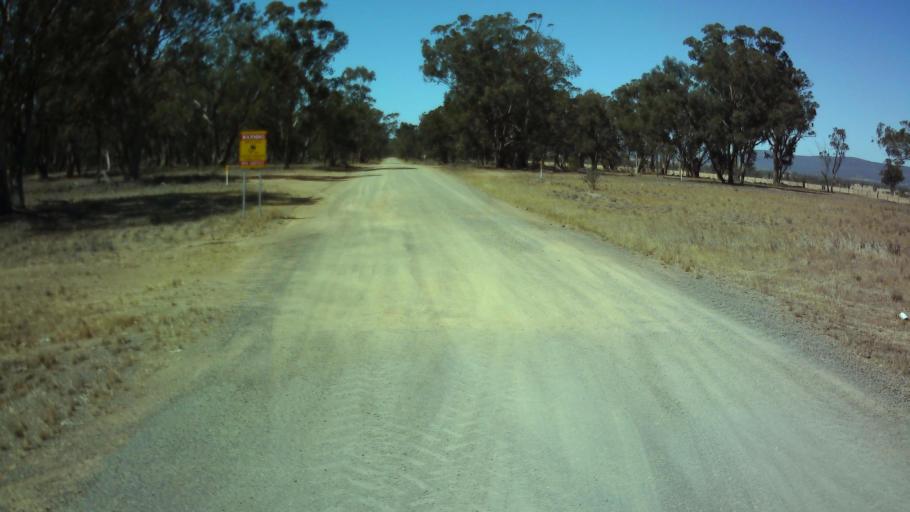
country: AU
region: New South Wales
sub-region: Weddin
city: Grenfell
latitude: -33.8492
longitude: 148.0886
